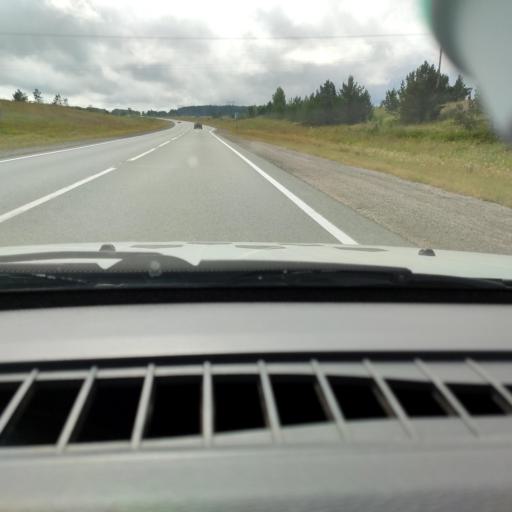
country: RU
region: Sverdlovsk
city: Achit
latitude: 56.8863
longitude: 57.6156
